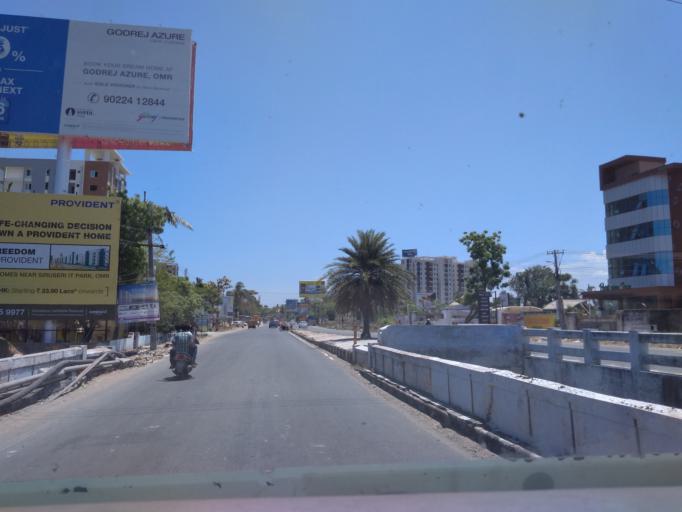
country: IN
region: Tamil Nadu
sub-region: Kancheepuram
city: Injambakkam
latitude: 12.8242
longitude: 80.2313
